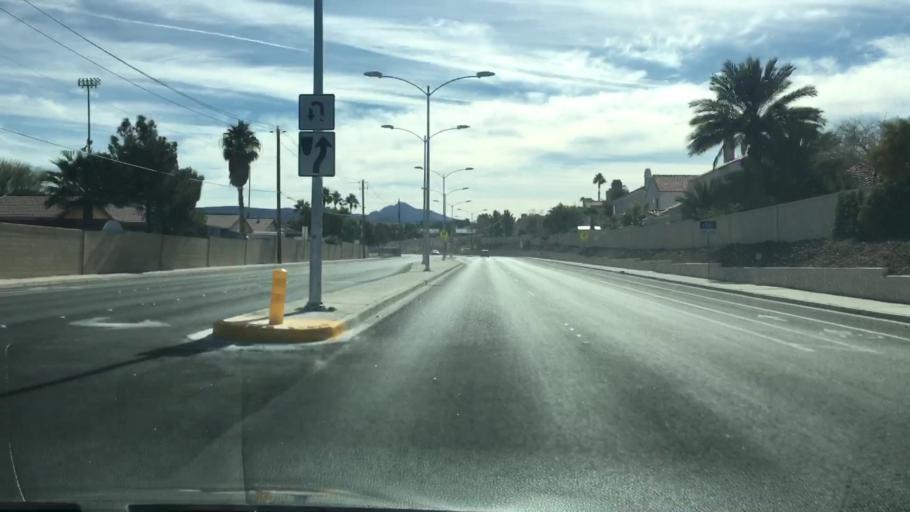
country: US
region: Nevada
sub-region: Clark County
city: Whitney
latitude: 36.0613
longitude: -115.0587
